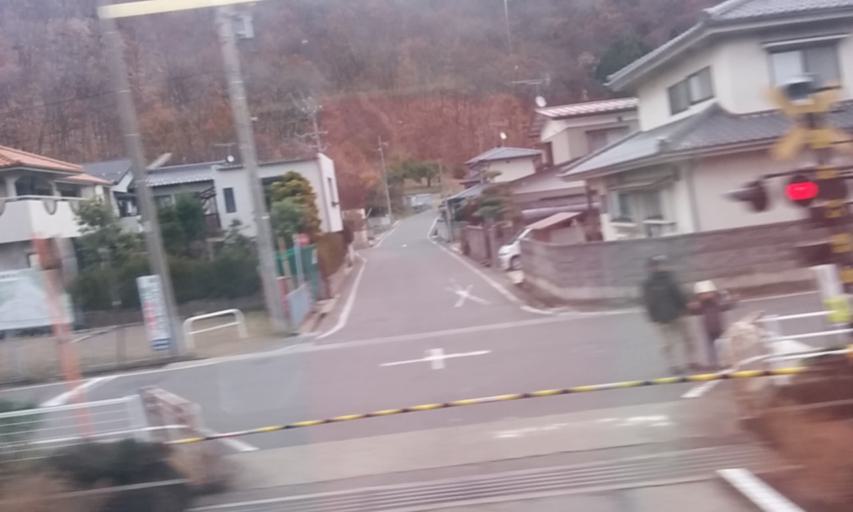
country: JP
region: Nagano
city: Nagano-shi
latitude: 36.5280
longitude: 138.1294
